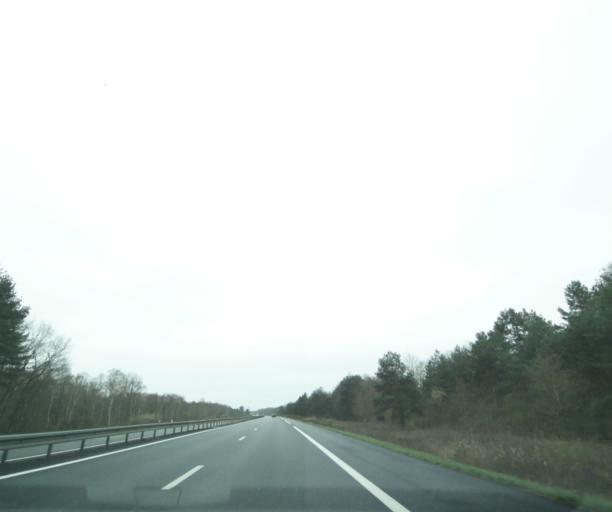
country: FR
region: Centre
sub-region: Departement du Loiret
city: Jouy-le-Potier
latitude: 47.7520
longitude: 1.8588
